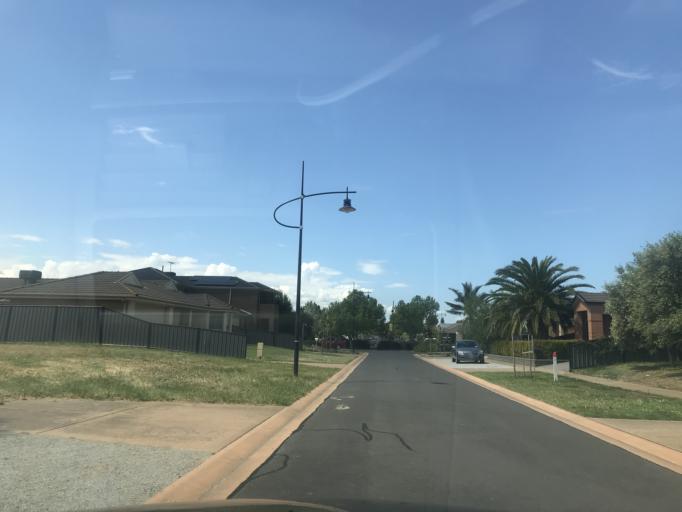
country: AU
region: Victoria
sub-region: Wyndham
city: Williams Landing
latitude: -37.8878
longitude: 144.7299
